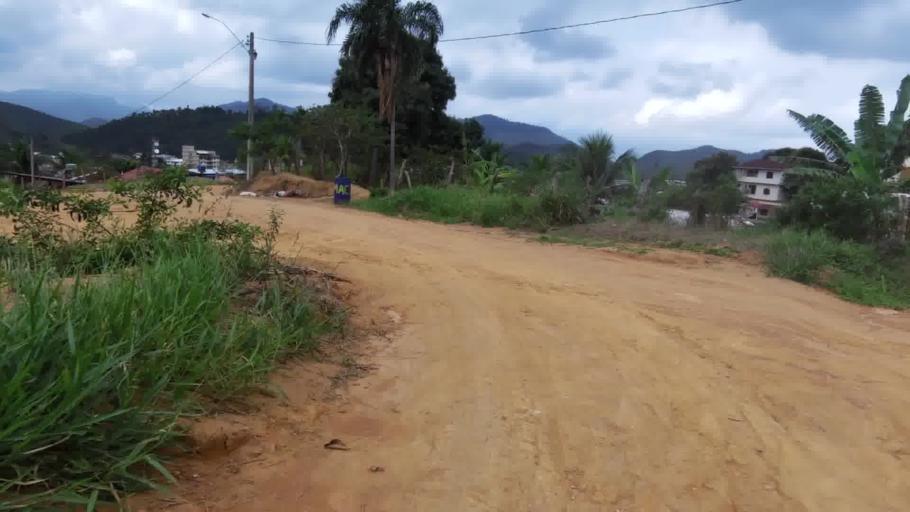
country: BR
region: Espirito Santo
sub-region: Alfredo Chaves
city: Alfredo Chaves
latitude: -20.6374
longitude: -40.7535
